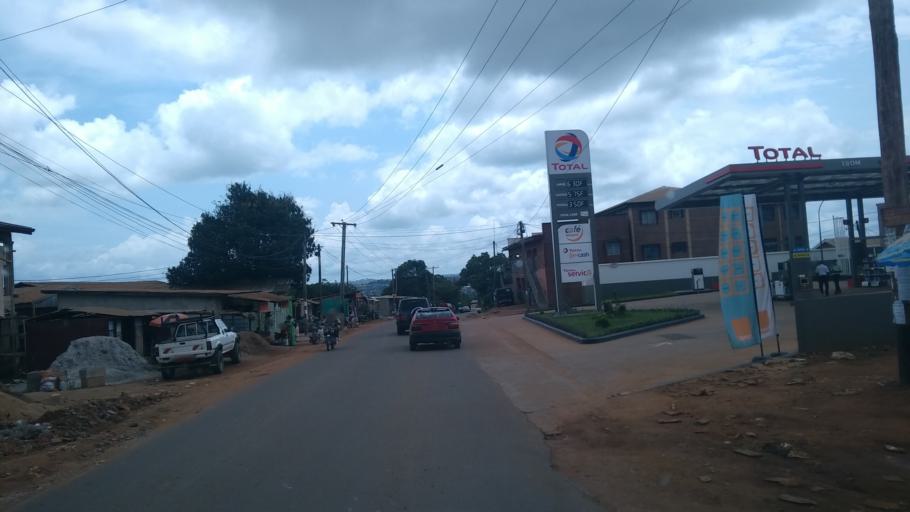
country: CM
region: Centre
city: Yaounde
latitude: 3.8103
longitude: 11.4907
